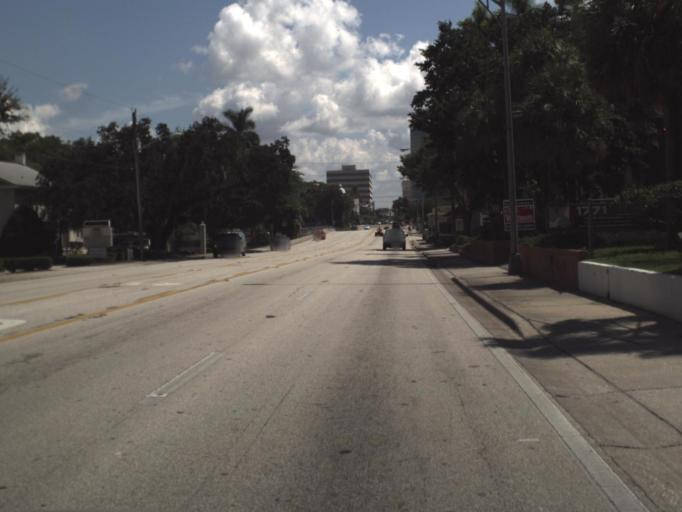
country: US
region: Florida
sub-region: Manatee County
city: Bradenton
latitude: 27.4955
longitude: -82.5799
